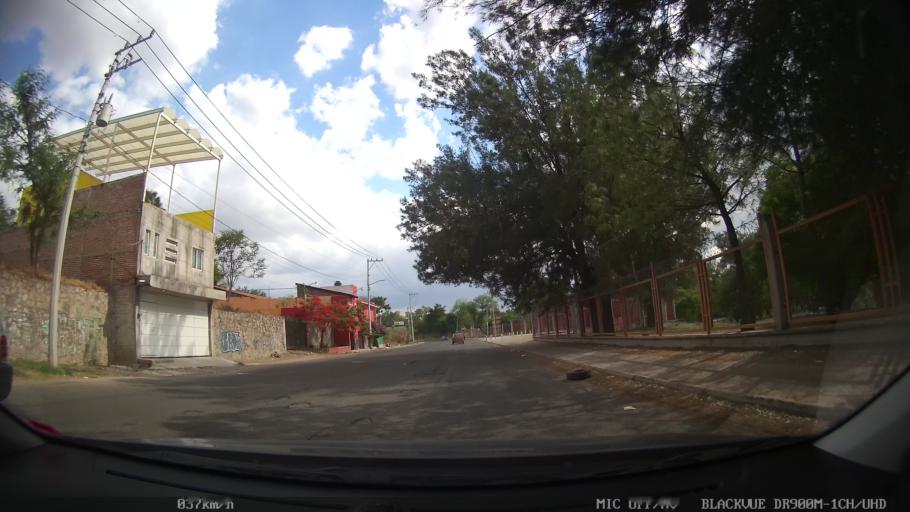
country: MX
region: Jalisco
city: Tlaquepaque
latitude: 20.6661
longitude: -103.2664
